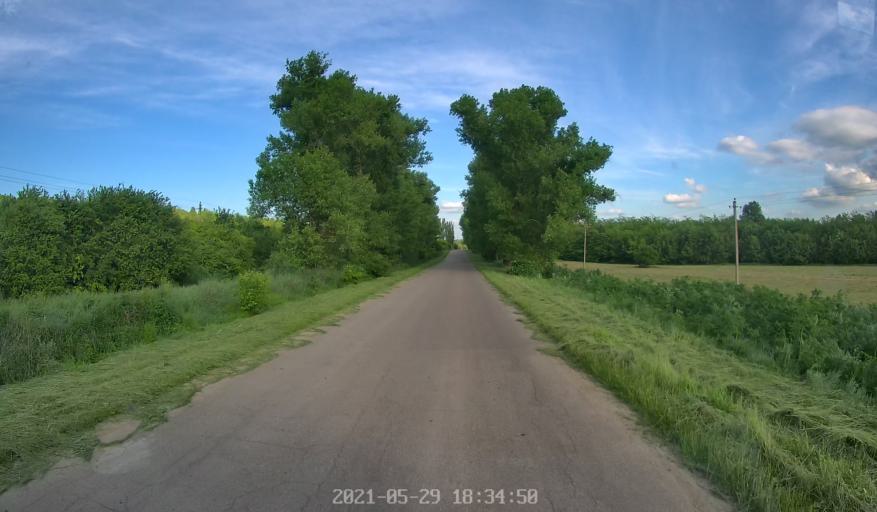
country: MD
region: Chisinau
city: Singera
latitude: 46.8114
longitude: 28.9153
